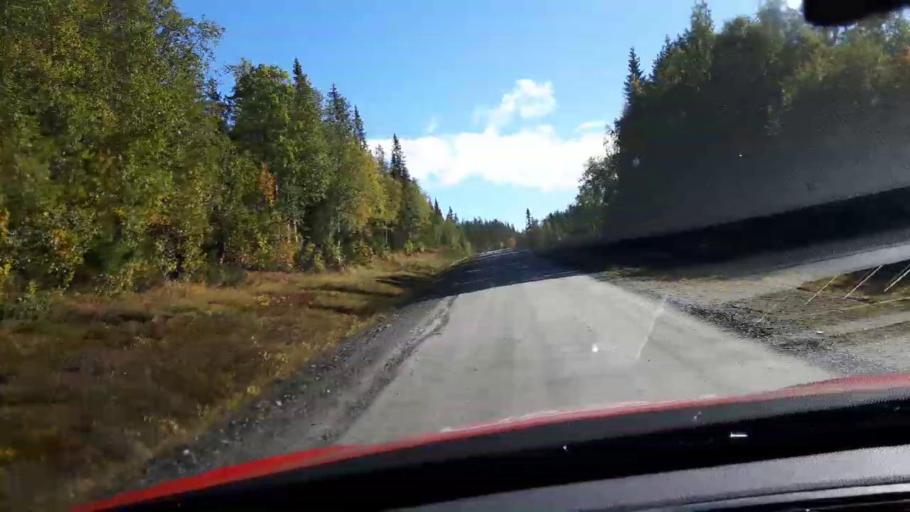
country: NO
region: Nord-Trondelag
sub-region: Lierne
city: Sandvika
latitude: 64.6119
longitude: 13.9470
